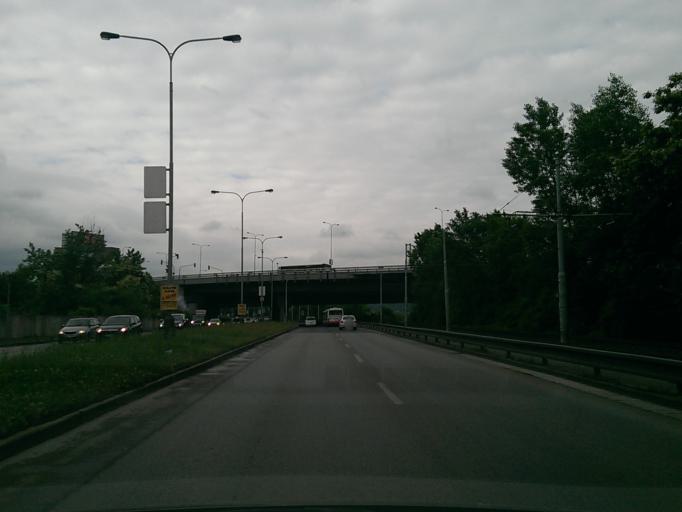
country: CZ
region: Praha
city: Branik
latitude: 50.0391
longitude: 14.4090
